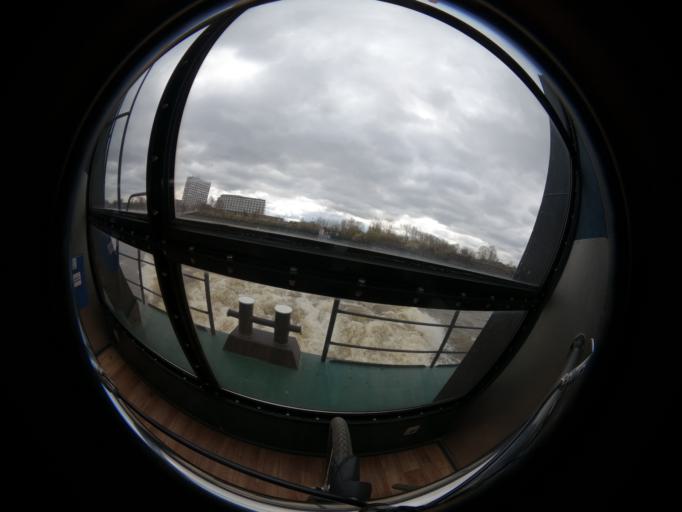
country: DE
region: Hamburg
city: Altona
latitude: 53.5429
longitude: 9.8612
